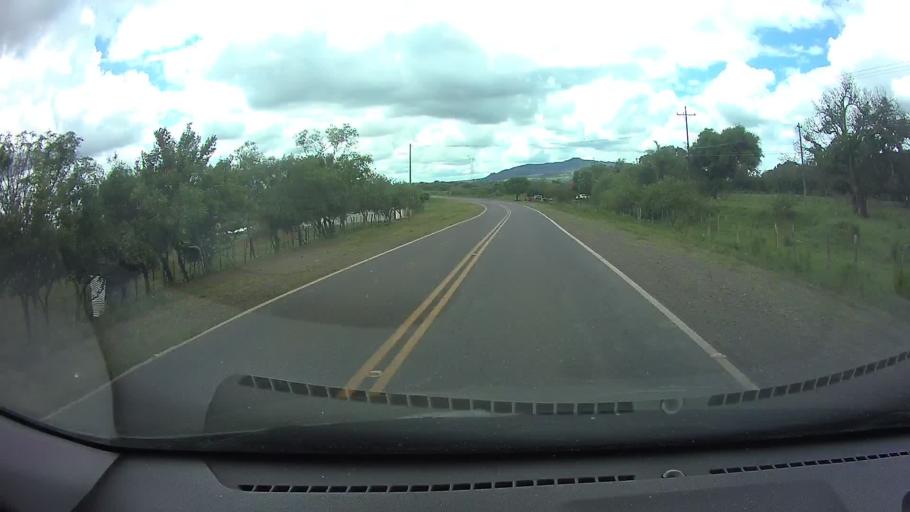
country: PY
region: Paraguari
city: Ybycui
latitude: -25.9134
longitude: -57.0297
